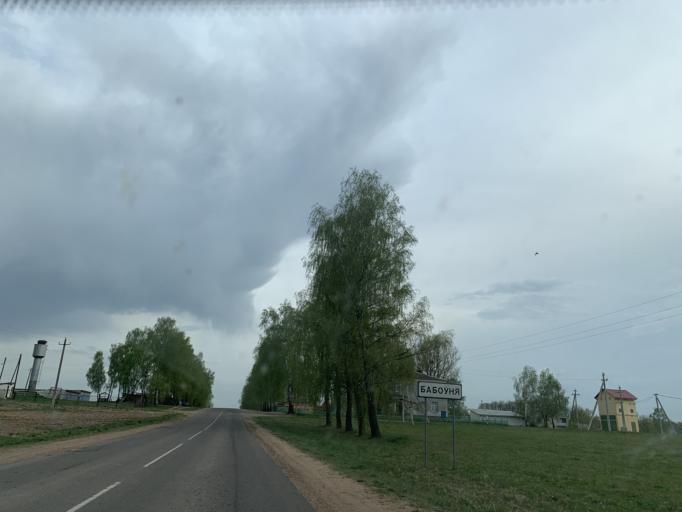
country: BY
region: Minsk
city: Kapyl'
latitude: 53.2647
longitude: 26.9572
